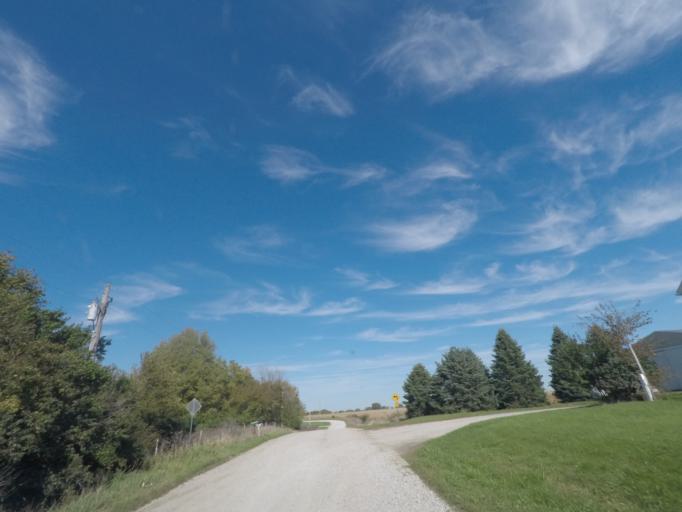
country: US
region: Iowa
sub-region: Story County
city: Nevada
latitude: 42.0104
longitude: -93.3476
